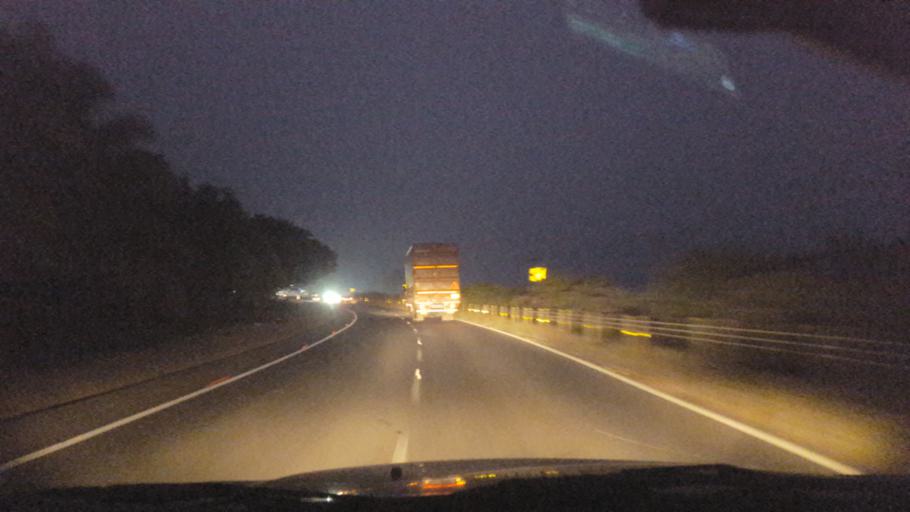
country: IN
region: Andhra Pradesh
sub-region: East Godavari
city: Peddapuram
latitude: 17.1371
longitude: 81.9667
